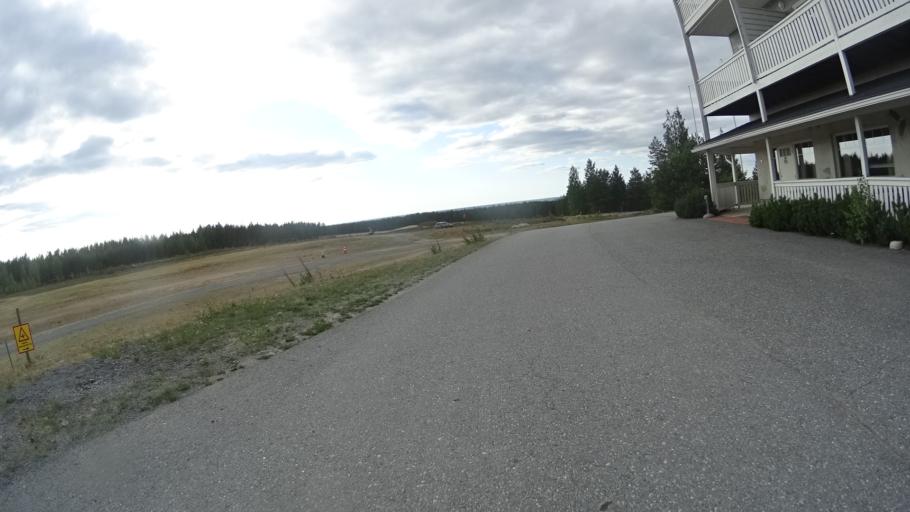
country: FI
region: Satakunta
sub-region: Pohjois-Satakunta
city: Jaemijaervi
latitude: 61.7783
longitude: 22.7154
